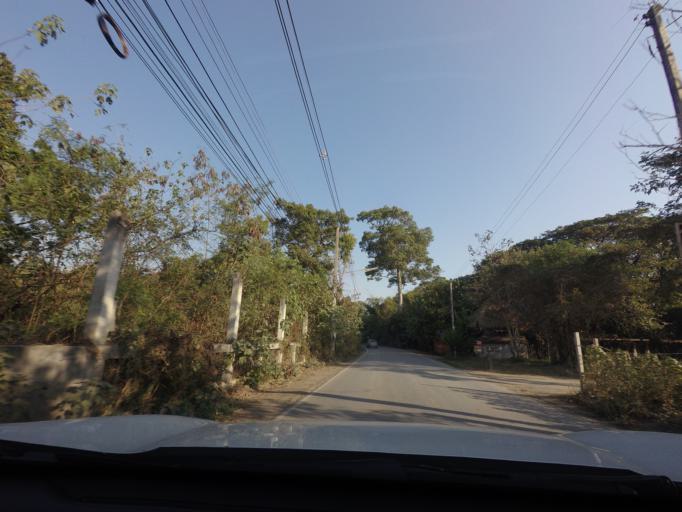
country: TH
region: Nakhon Ratchasima
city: Pak Chong
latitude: 14.6162
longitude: 101.4447
